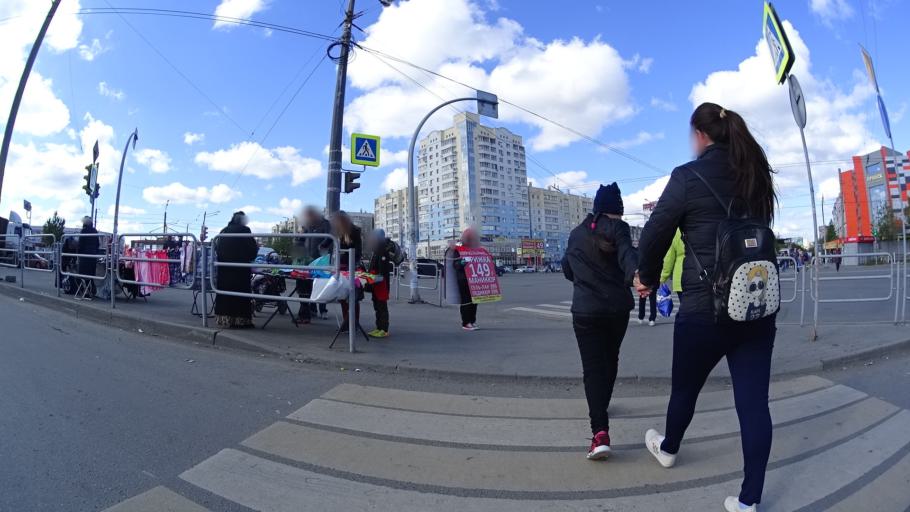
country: RU
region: Chelyabinsk
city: Roshchino
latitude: 55.1822
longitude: 61.2923
